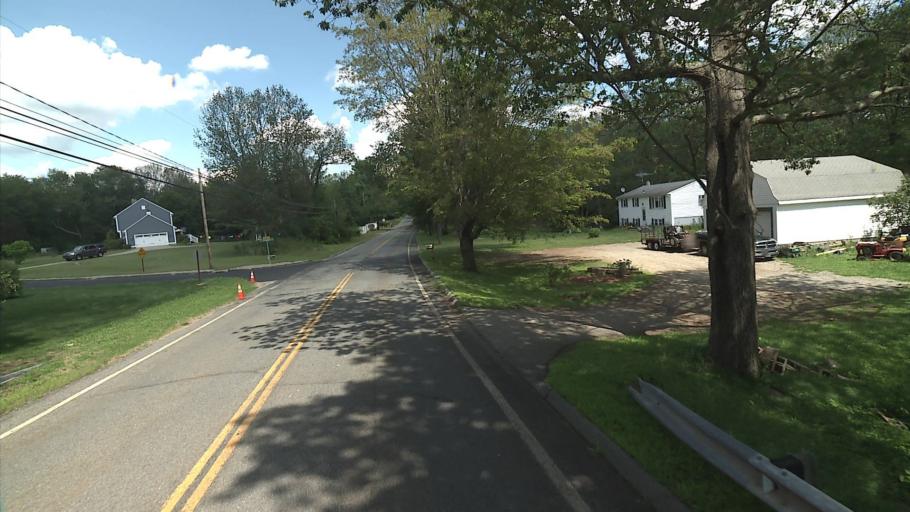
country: US
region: Connecticut
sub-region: Tolland County
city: Mansfield City
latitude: 41.7922
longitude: -72.1757
